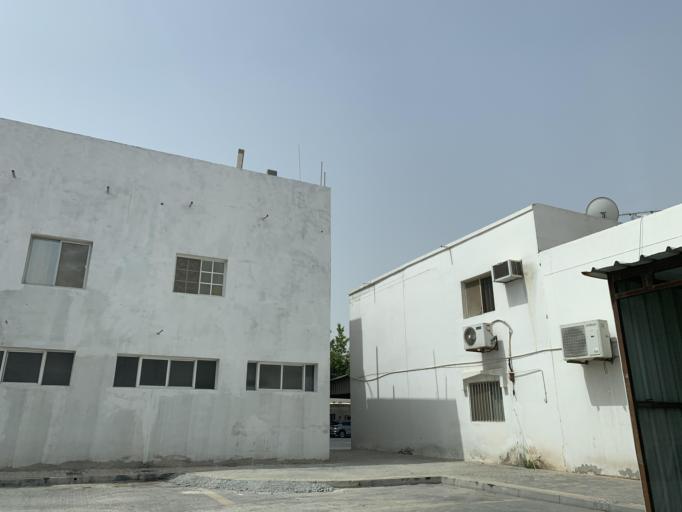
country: BH
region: Northern
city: Madinat `Isa
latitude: 26.1661
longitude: 50.5570
